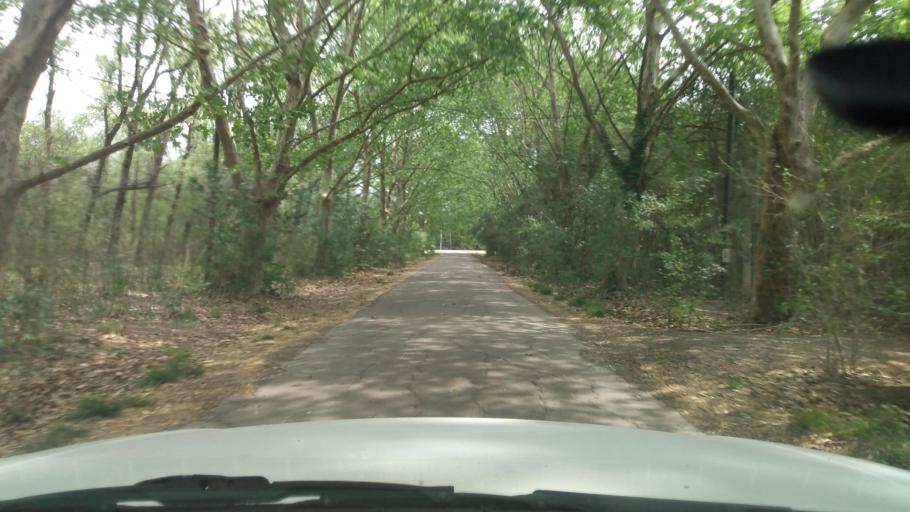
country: AR
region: Buenos Aires
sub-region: Partido de Lujan
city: Lujan
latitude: -34.5567
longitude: -59.1906
